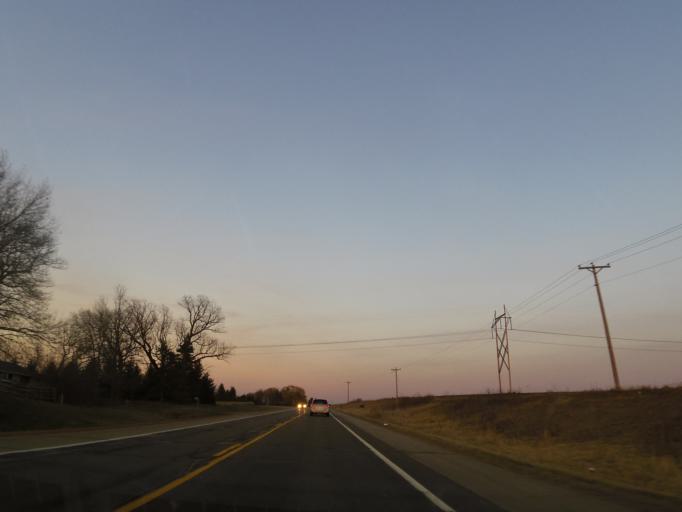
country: US
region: Minnesota
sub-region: Scott County
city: Jordan
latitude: 44.6742
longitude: -93.5788
